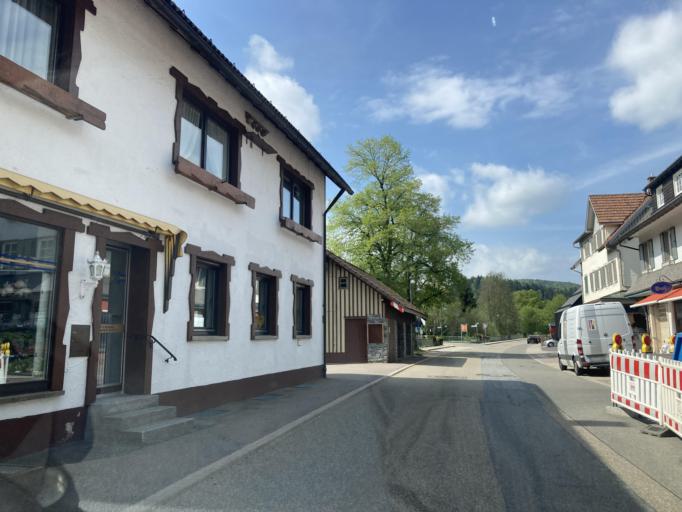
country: DE
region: Baden-Wuerttemberg
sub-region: Karlsruhe Region
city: Biberach
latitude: 48.5317
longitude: 8.2836
